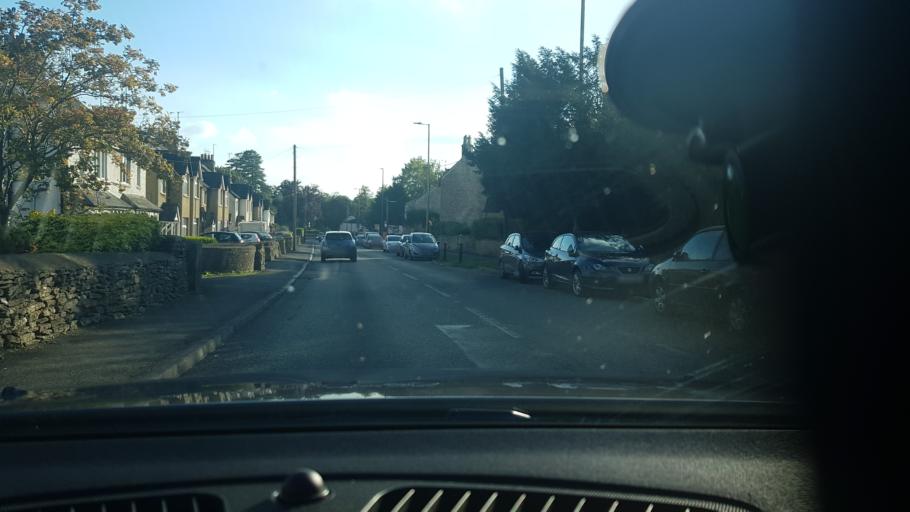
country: GB
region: England
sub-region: Gloucestershire
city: Cirencester
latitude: 51.7286
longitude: -1.9755
